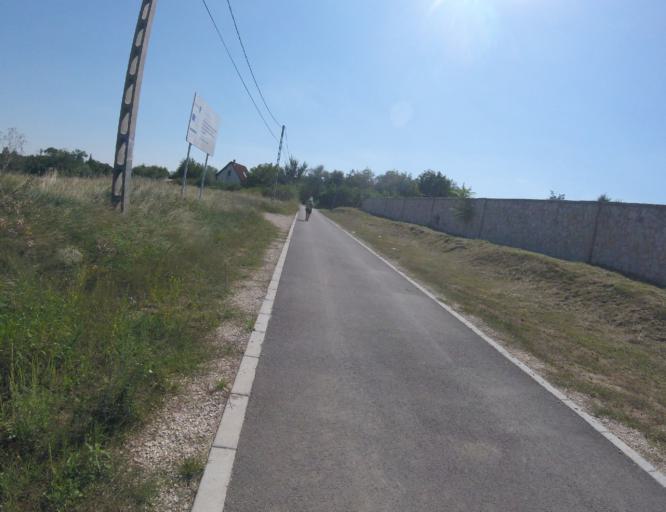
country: HU
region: Fejer
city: Velence
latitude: 47.2539
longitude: 18.6117
